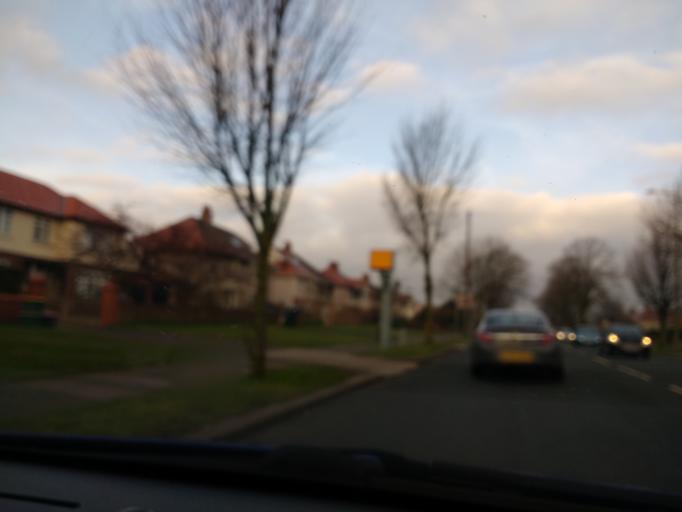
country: GB
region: England
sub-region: Lancashire
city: Morecambe
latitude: 54.0642
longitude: -2.8341
